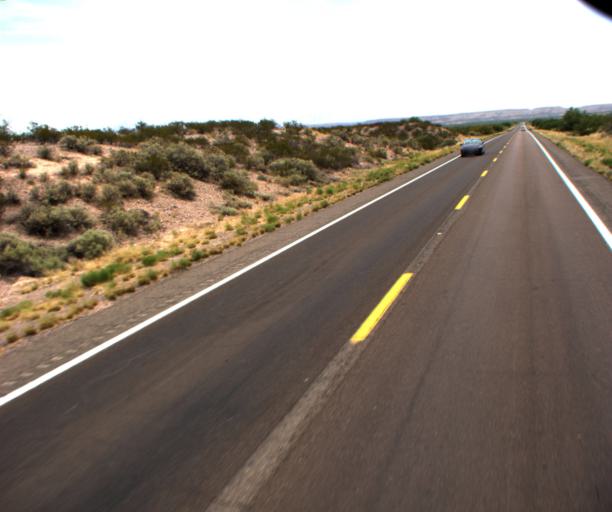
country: US
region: Arizona
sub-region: Graham County
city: Bylas
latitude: 33.1855
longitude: -110.1610
